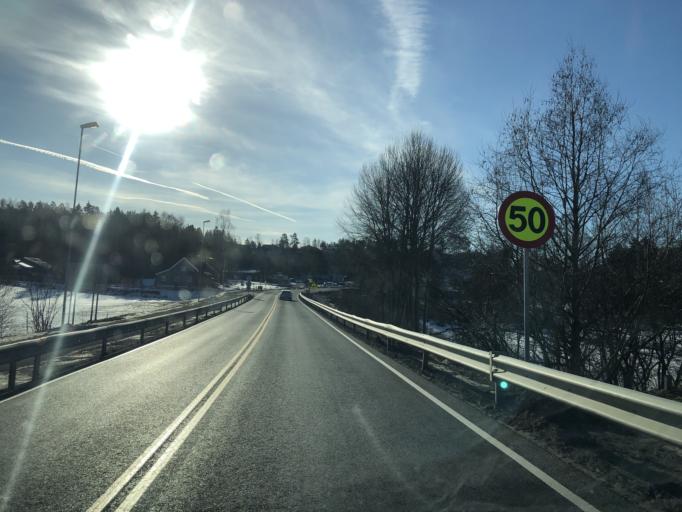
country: NO
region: Hedmark
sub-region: Ringsaker
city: Moelv
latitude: 60.9160
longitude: 10.7074
